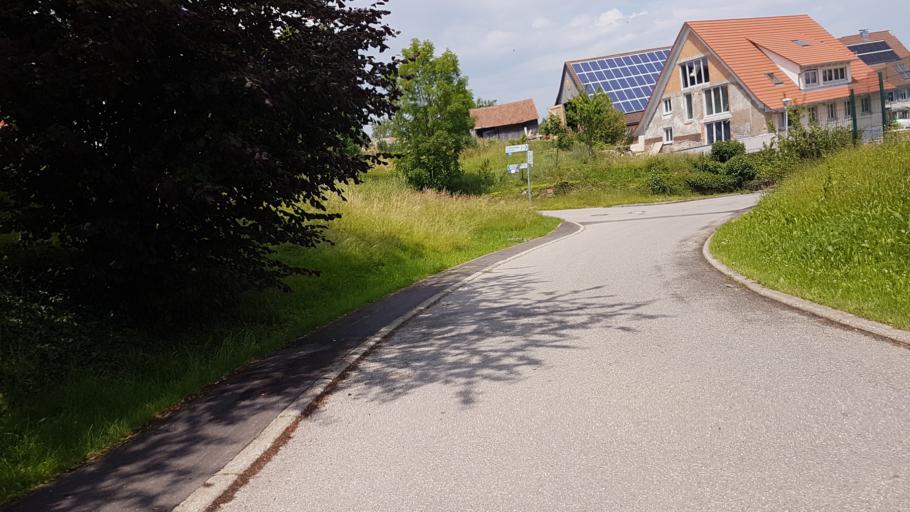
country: DE
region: Baden-Wuerttemberg
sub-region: Freiburg Region
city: Hufingen
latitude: 47.8932
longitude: 8.4863
